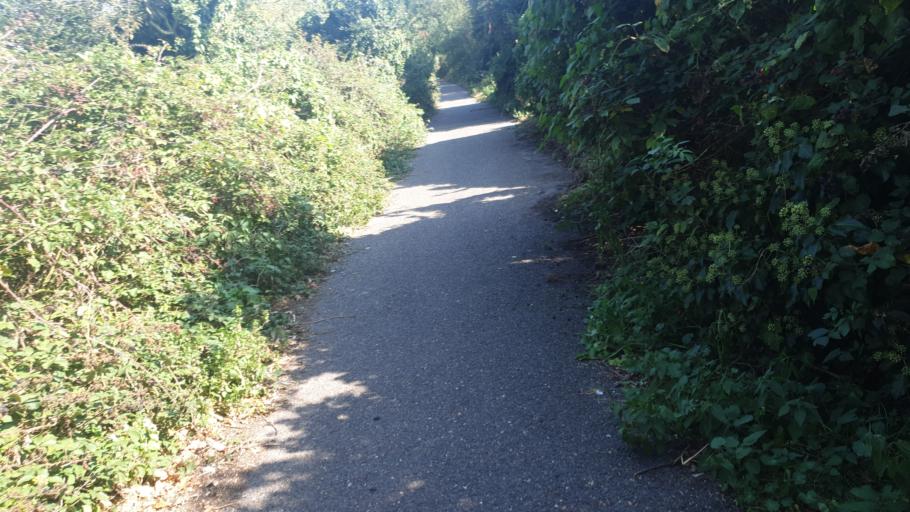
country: GB
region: England
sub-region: Essex
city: Dovercourt
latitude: 51.9387
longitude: 1.2643
